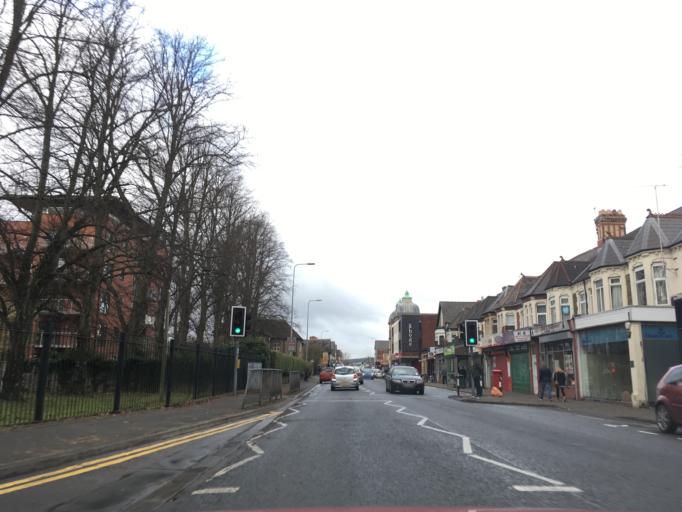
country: GB
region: Wales
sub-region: Cardiff
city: Cardiff
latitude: 51.5006
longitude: -3.1873
